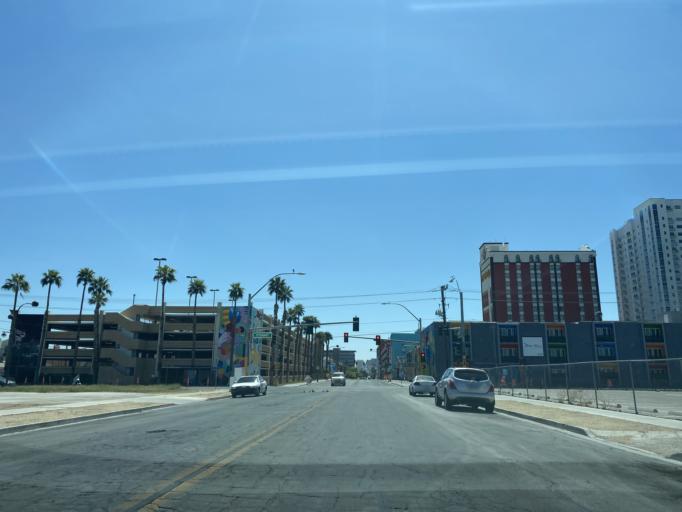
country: US
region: Nevada
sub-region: Clark County
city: Las Vegas
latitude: 36.1711
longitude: -115.1367
